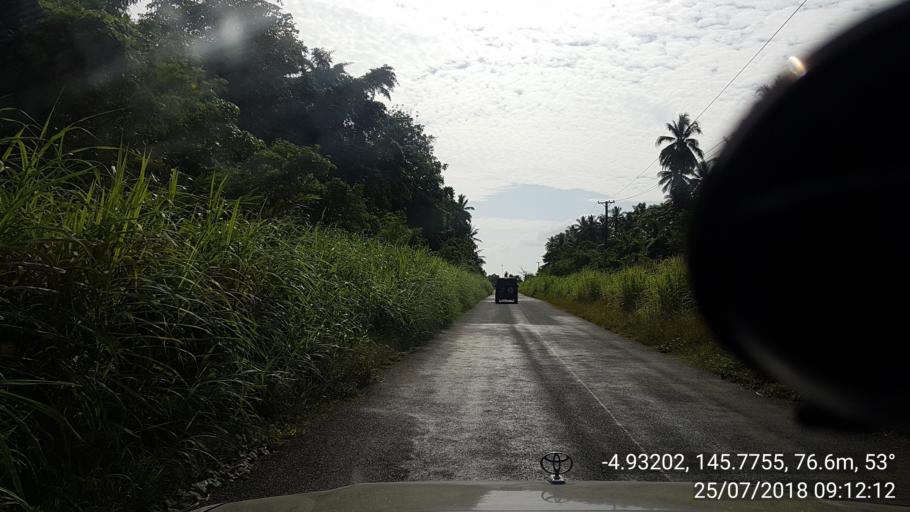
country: PG
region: Madang
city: Madang
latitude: -4.9315
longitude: 145.7764
